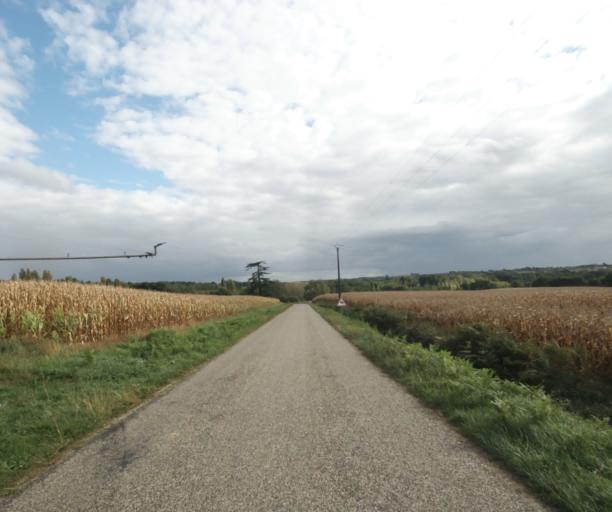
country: FR
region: Midi-Pyrenees
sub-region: Departement du Gers
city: Eauze
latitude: 43.8870
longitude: 0.0995
